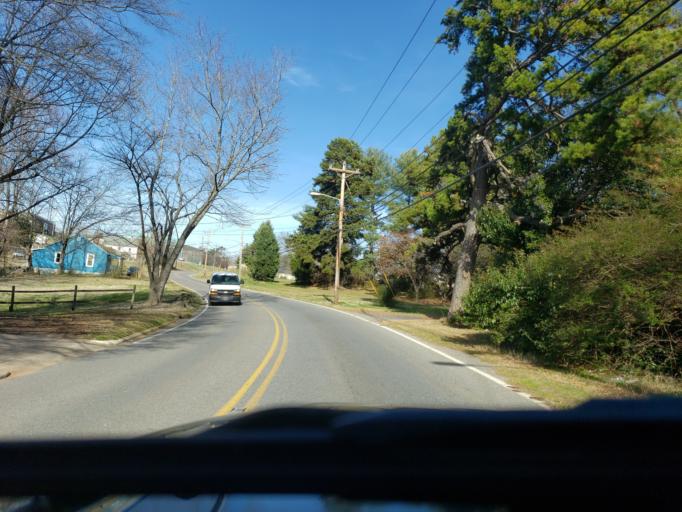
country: US
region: North Carolina
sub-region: Cleveland County
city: Kings Mountain
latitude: 35.2563
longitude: -81.3371
